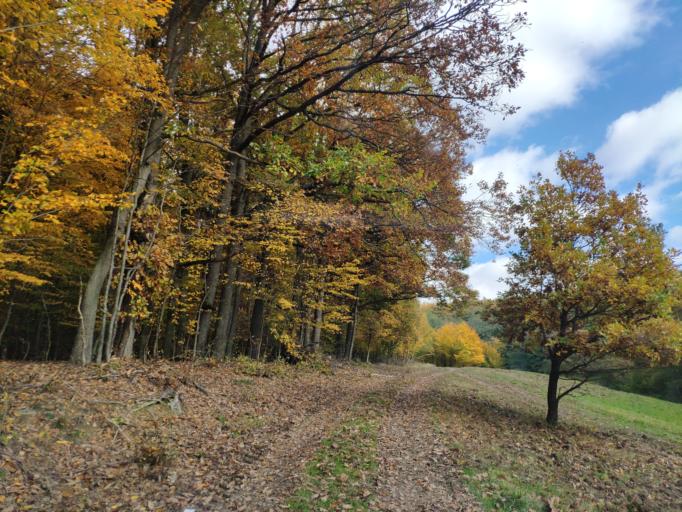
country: SK
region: Kosicky
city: Medzev
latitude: 48.7195
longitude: 20.9927
